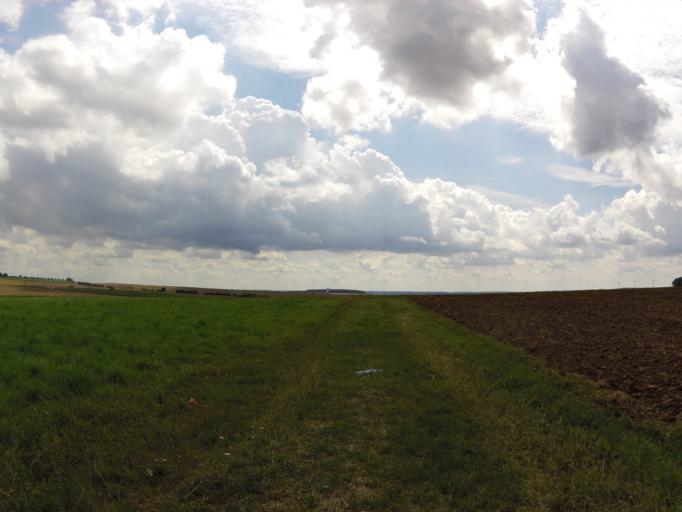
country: DE
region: Bavaria
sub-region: Regierungsbezirk Unterfranken
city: Geroldshausen
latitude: 49.6975
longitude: 9.8799
